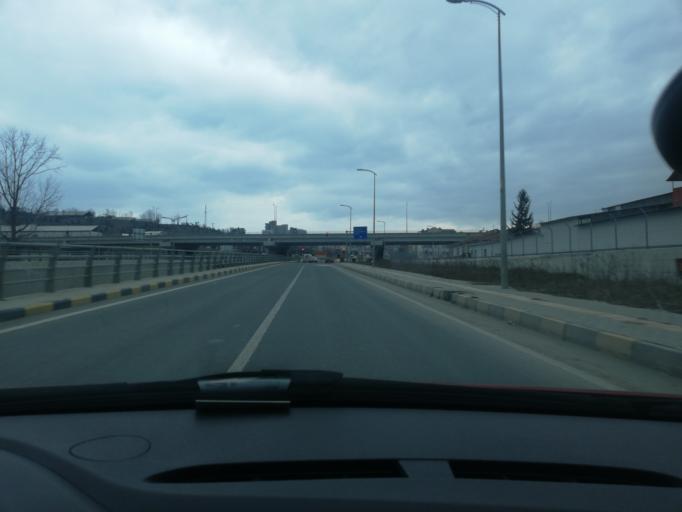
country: TR
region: Kastamonu
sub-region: Cide
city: Kastamonu
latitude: 41.4153
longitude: 33.7988
